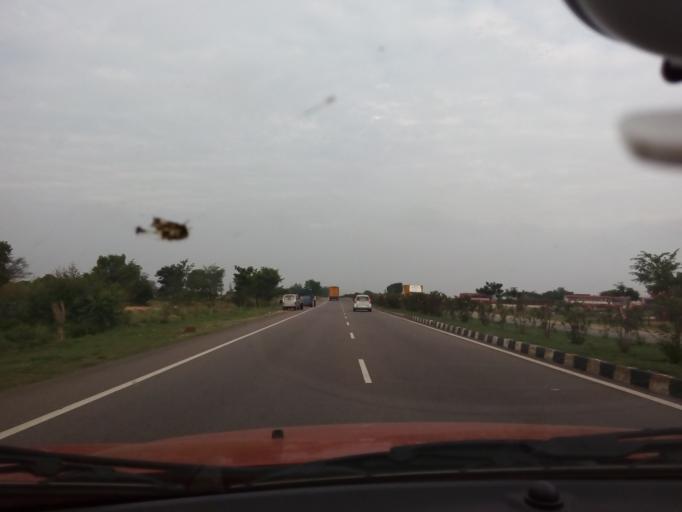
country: IN
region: Karnataka
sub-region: Tumkur
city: Kunigal
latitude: 12.9968
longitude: 76.9254
